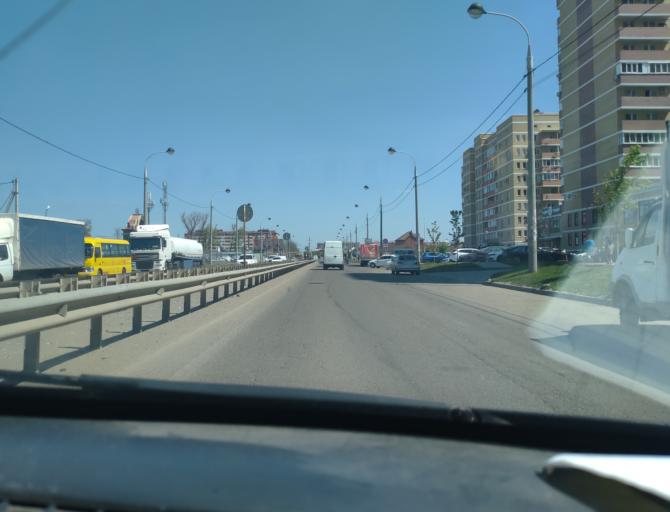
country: RU
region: Krasnodarskiy
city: Krasnodar
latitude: 45.0944
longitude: 39.0098
